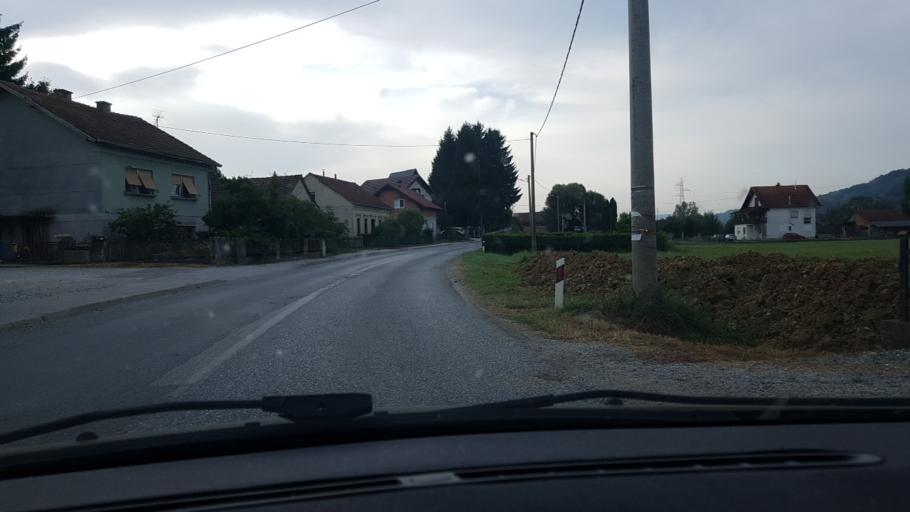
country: HR
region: Krapinsko-Zagorska
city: Zlatar
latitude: 46.0958
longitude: 16.0390
